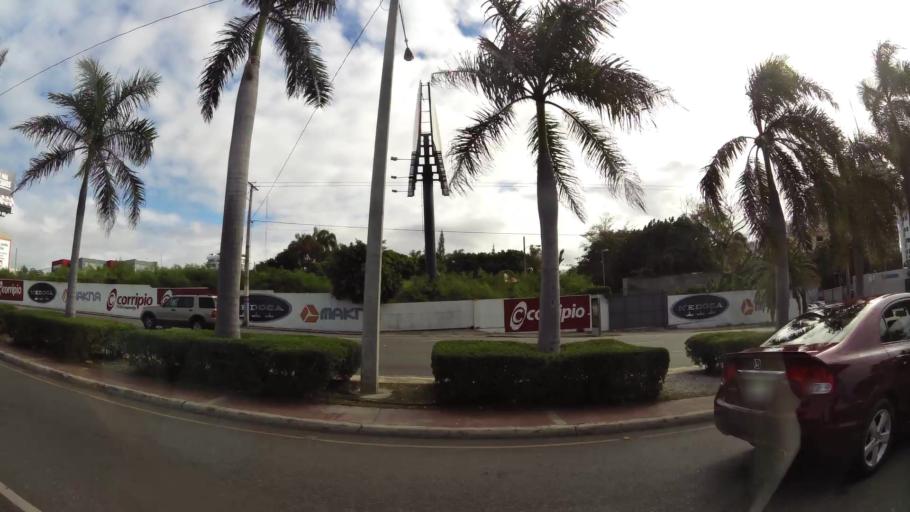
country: DO
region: Nacional
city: La Julia
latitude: 18.4619
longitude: -69.9350
